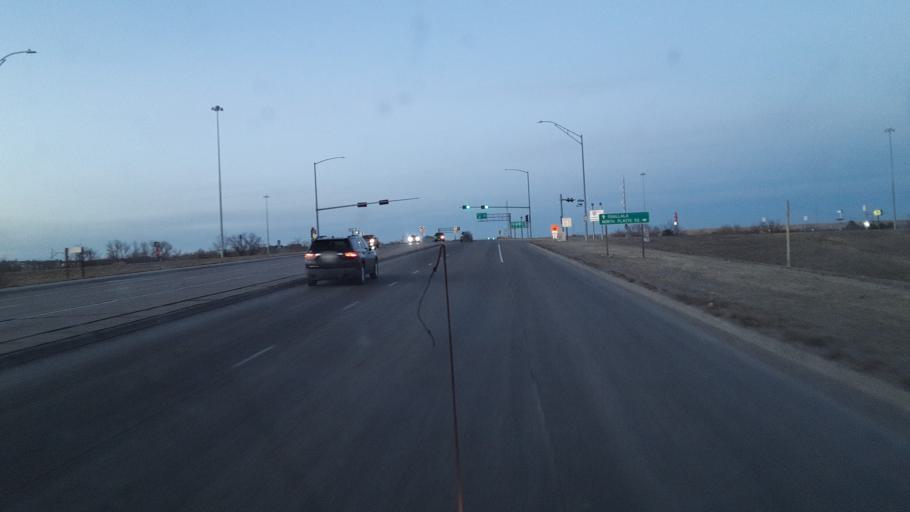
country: US
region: Nebraska
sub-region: Keith County
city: Ogallala
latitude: 41.1126
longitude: -101.7156
